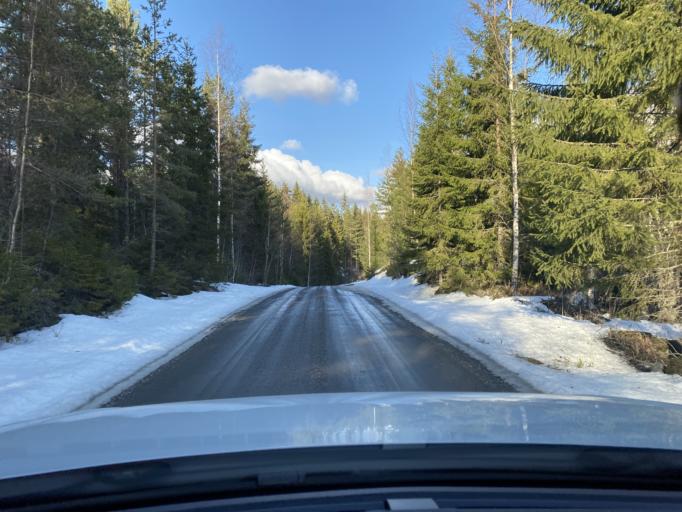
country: FI
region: Pirkanmaa
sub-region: Lounais-Pirkanmaa
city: Mouhijaervi
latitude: 61.4551
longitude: 22.9302
